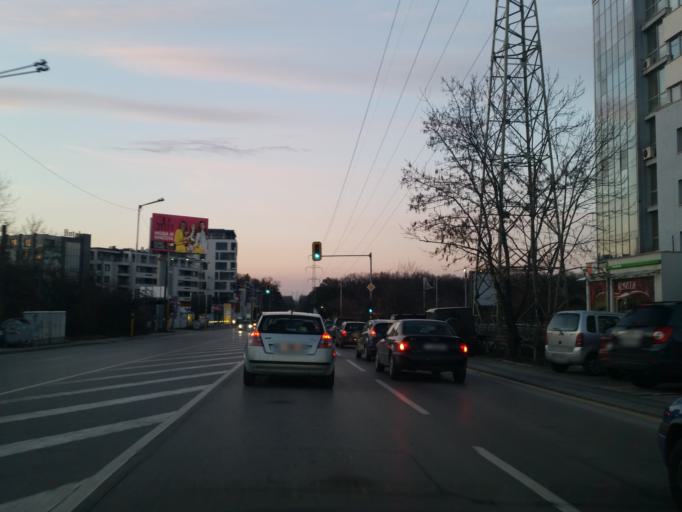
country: BG
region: Sofia-Capital
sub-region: Stolichna Obshtina
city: Sofia
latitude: 42.6569
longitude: 23.3364
